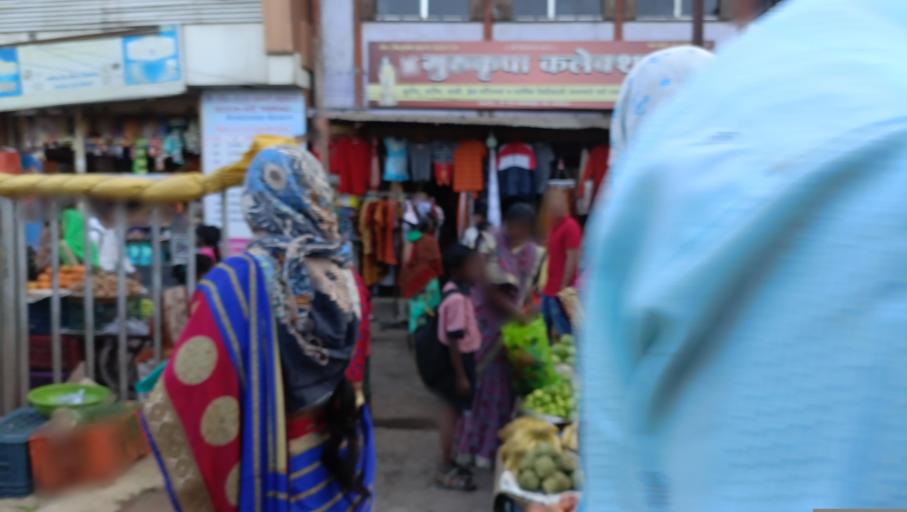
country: IN
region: Maharashtra
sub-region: Nashik Division
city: Trimbak
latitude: 19.9331
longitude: 73.5291
